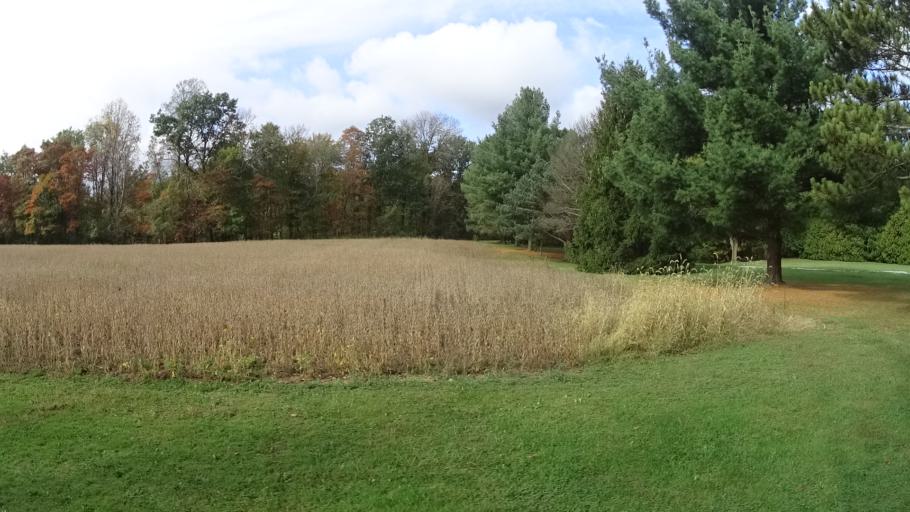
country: US
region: Ohio
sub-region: Lorain County
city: Grafton
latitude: 41.3040
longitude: -82.0813
